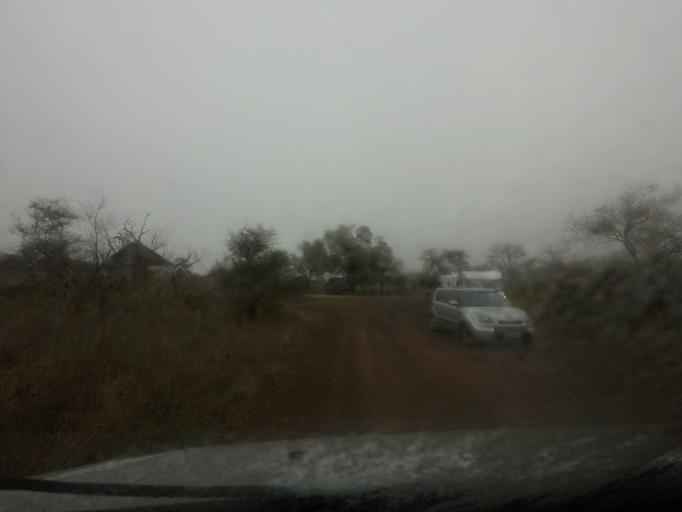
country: ZA
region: Limpopo
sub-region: Mopani District Municipality
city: Phalaborwa
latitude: -24.2608
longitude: 31.6456
